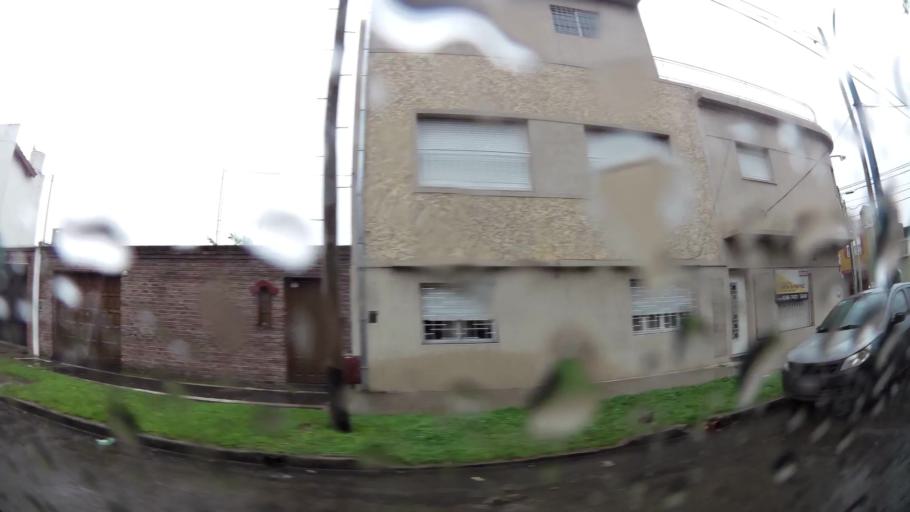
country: AR
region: Buenos Aires
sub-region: Partido de Lanus
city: Lanus
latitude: -34.7156
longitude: -58.4046
